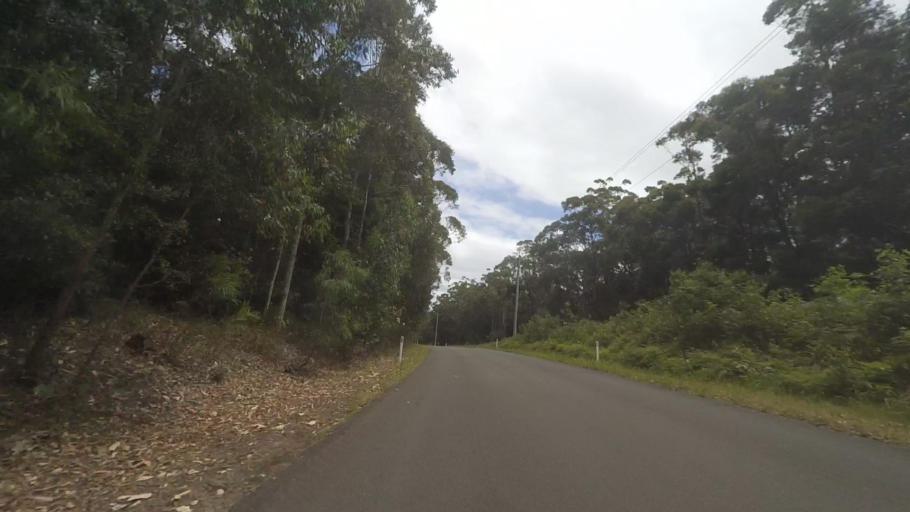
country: AU
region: New South Wales
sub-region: Shoalhaven Shire
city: Milton
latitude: -35.3771
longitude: 150.3756
